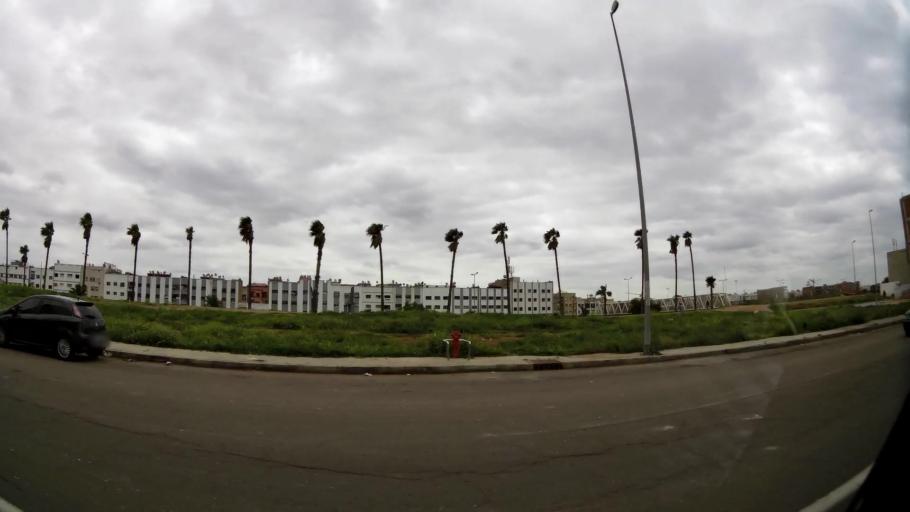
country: MA
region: Grand Casablanca
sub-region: Casablanca
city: Casablanca
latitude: 33.5825
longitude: -7.5500
